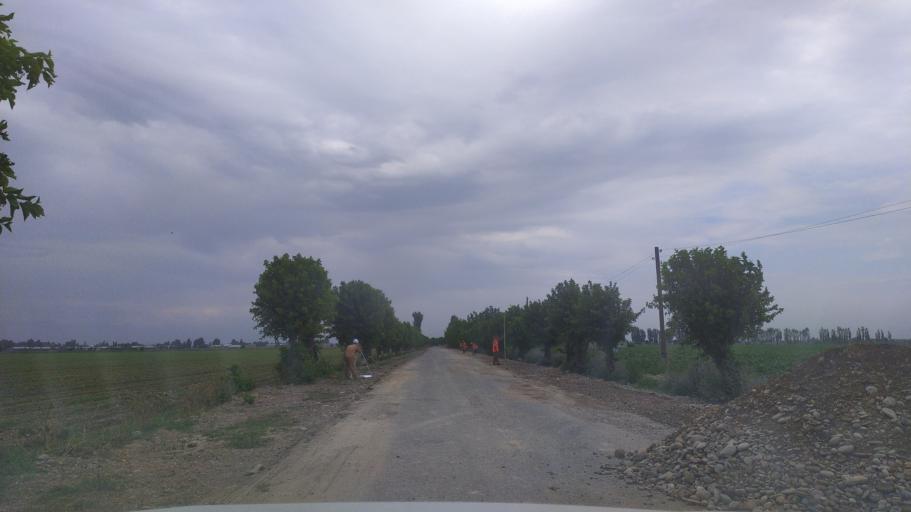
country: UZ
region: Namangan
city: Uychi
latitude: 41.0599
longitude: 71.9576
